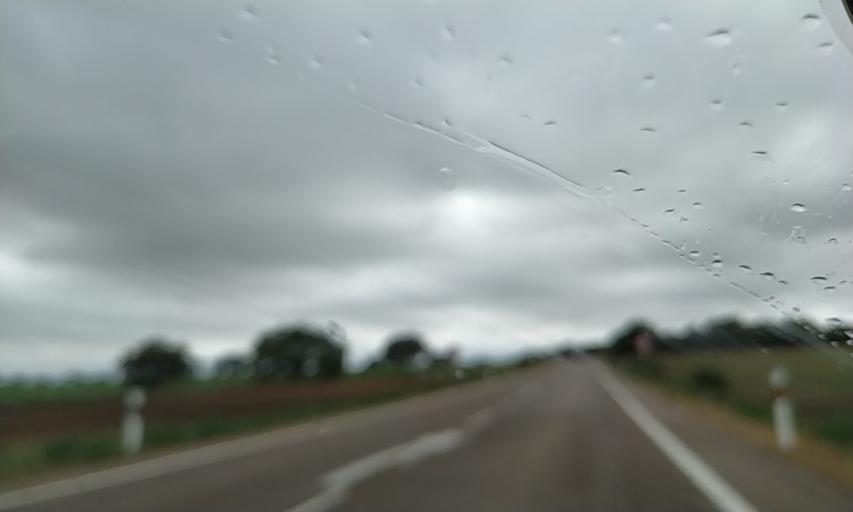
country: ES
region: Extremadura
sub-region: Provincia de Badajoz
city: Villar del Rey
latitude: 39.0482
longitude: -6.8032
